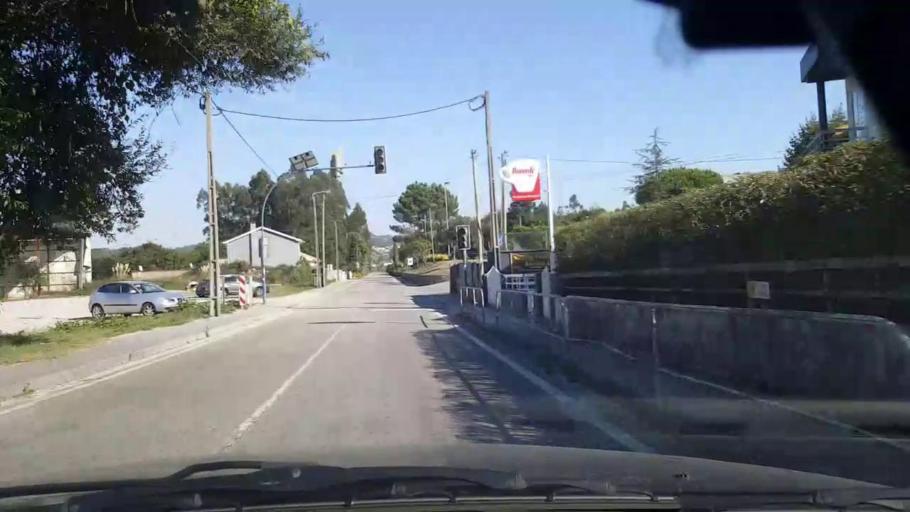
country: PT
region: Porto
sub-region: Vila do Conde
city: Arvore
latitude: 41.3368
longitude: -8.6789
